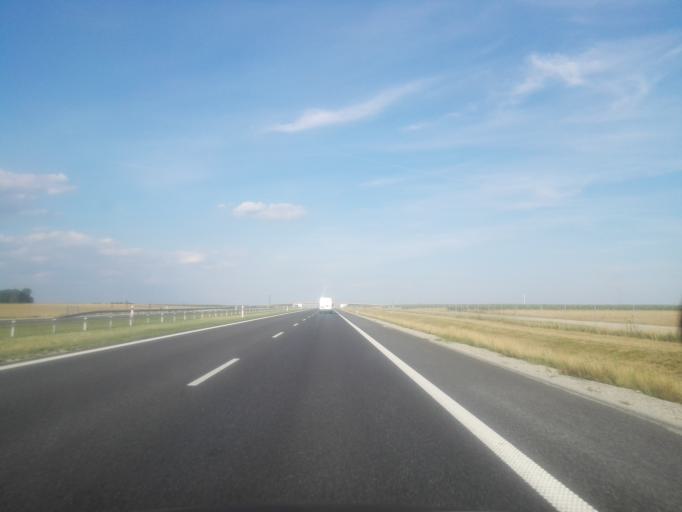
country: PL
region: Greater Poland Voivodeship
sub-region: Powiat kepinski
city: Kepno
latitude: 51.3171
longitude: 18.0319
